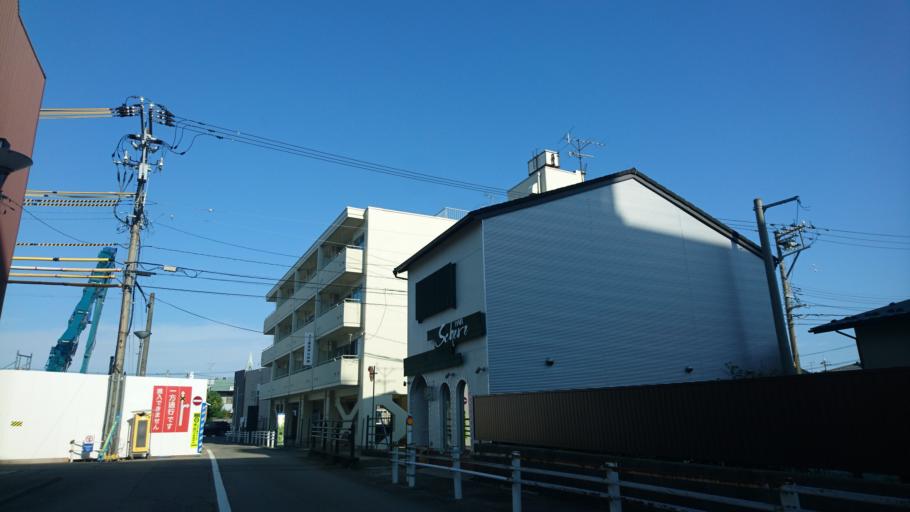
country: JP
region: Ishikawa
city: Komatsu
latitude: 36.2901
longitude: 136.3584
